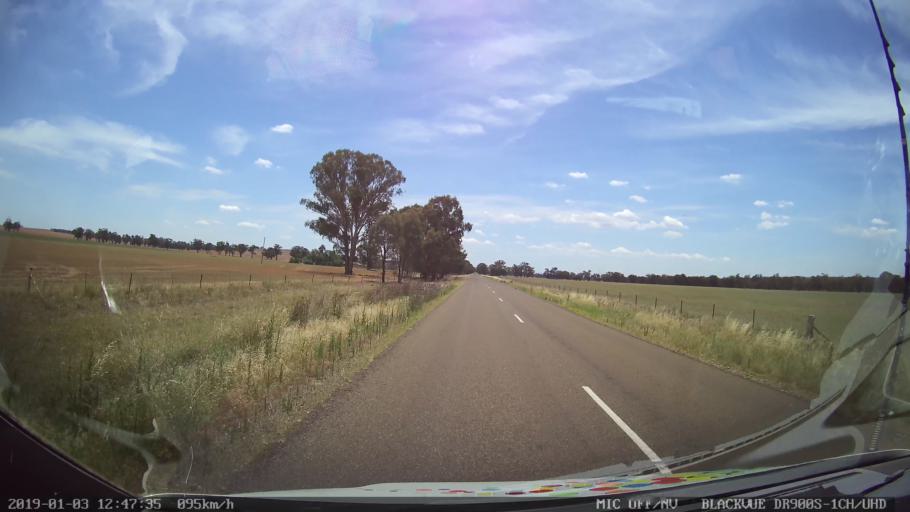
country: AU
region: New South Wales
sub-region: Weddin
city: Grenfell
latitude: -33.7250
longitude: 148.2431
